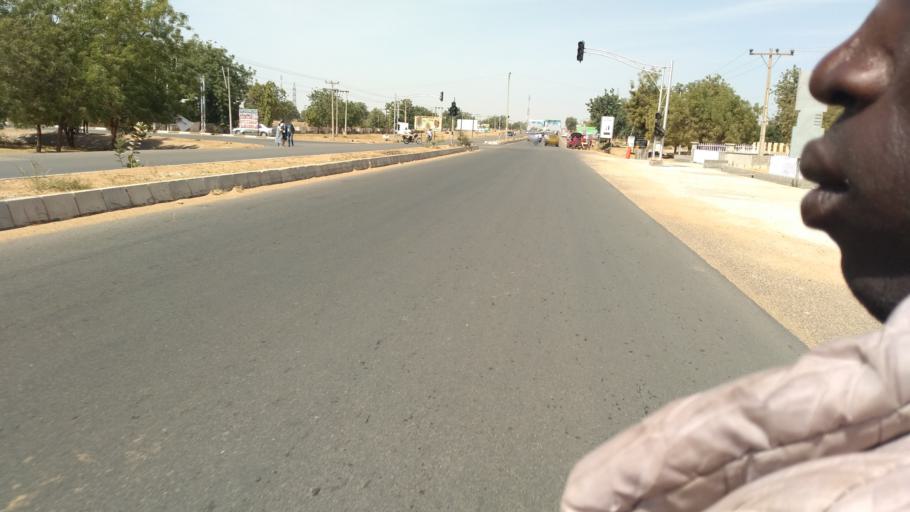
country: NG
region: Jigawa
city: Dutse
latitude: 11.6843
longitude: 9.3396
